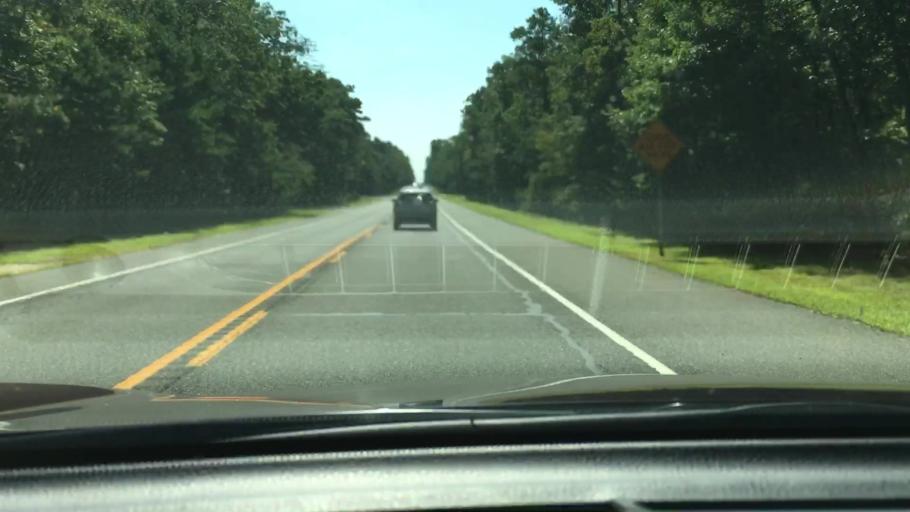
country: US
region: New Jersey
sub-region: Cumberland County
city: Laurel Lake
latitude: 39.3507
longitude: -74.9093
